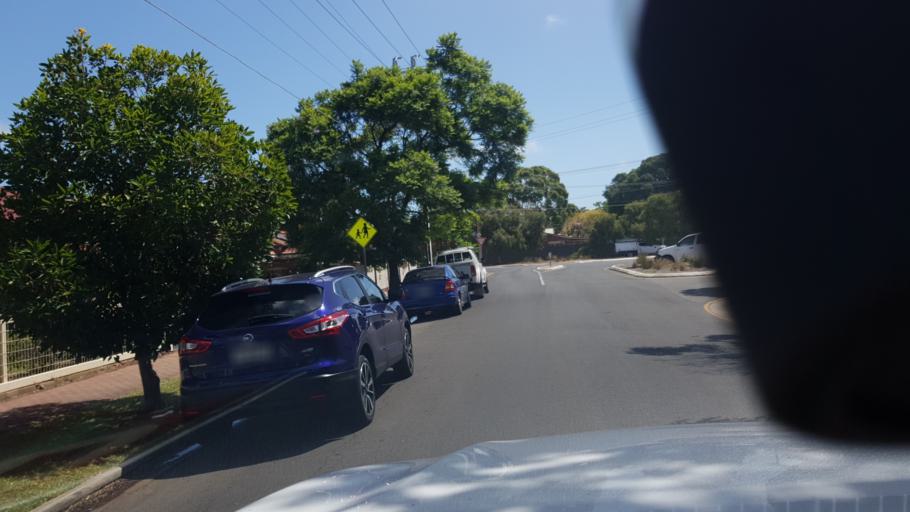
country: AU
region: South Australia
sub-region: Adelaide
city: Glenelg
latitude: -34.9856
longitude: 138.5243
